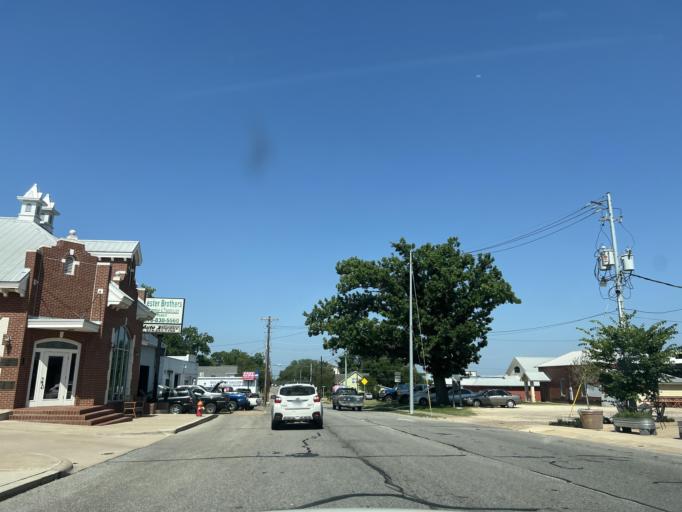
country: US
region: Texas
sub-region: Washington County
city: Brenham
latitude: 30.1671
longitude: -96.3961
